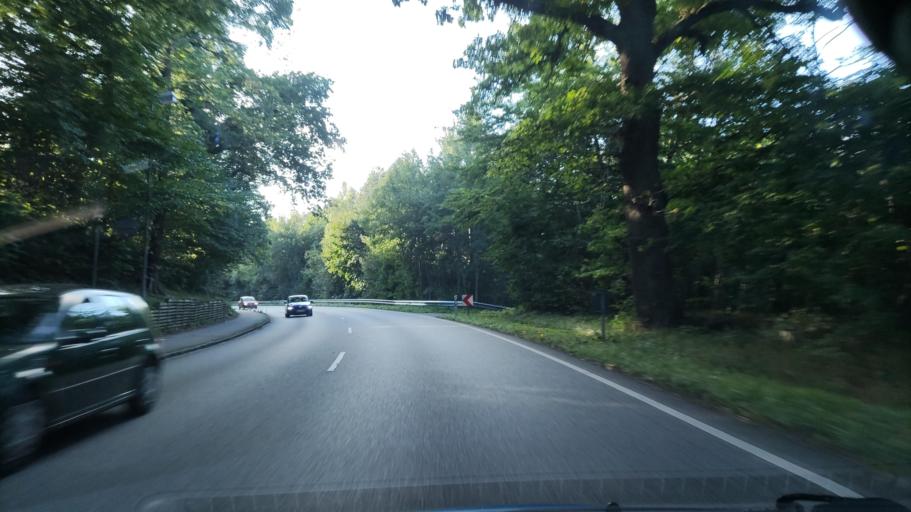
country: DE
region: Schleswig-Holstein
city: Bosdorf
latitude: 54.1452
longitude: 10.4628
